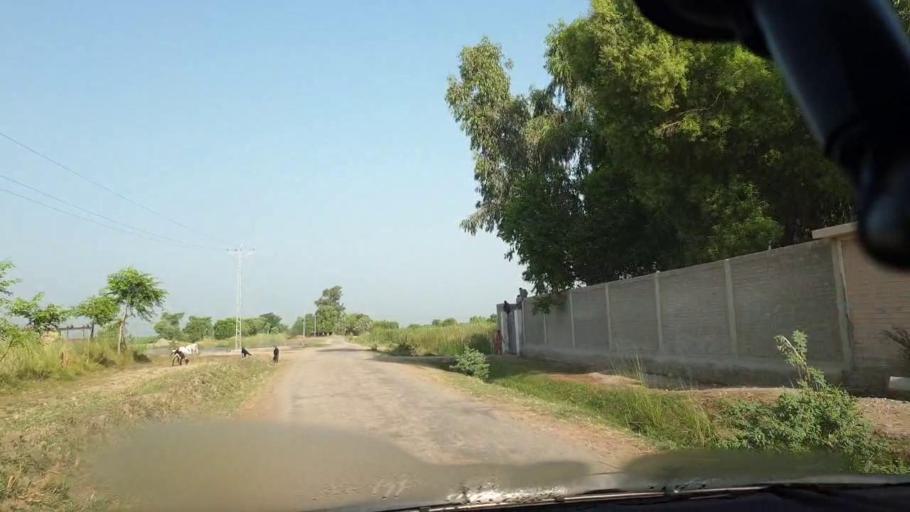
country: PK
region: Sindh
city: Larkana
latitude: 27.6189
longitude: 68.2151
